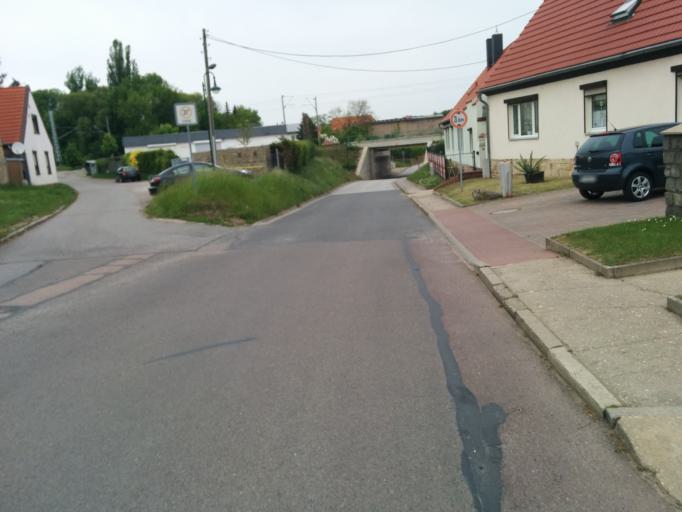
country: DE
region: Saxony-Anhalt
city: Zscherben
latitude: 51.4641
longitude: 11.8713
